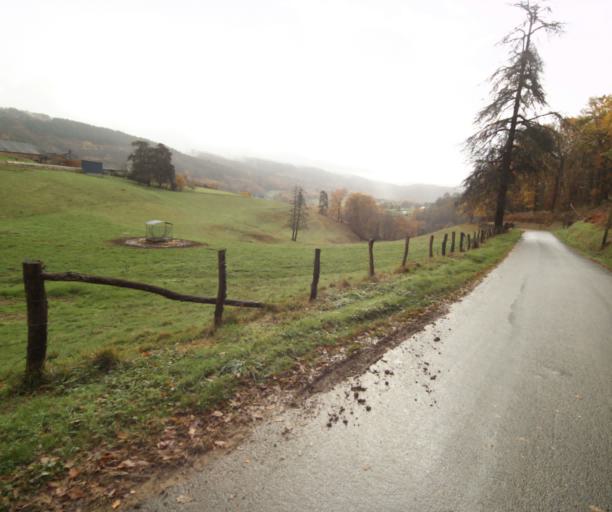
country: FR
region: Limousin
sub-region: Departement de la Correze
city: Cornil
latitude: 45.2042
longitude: 1.6511
